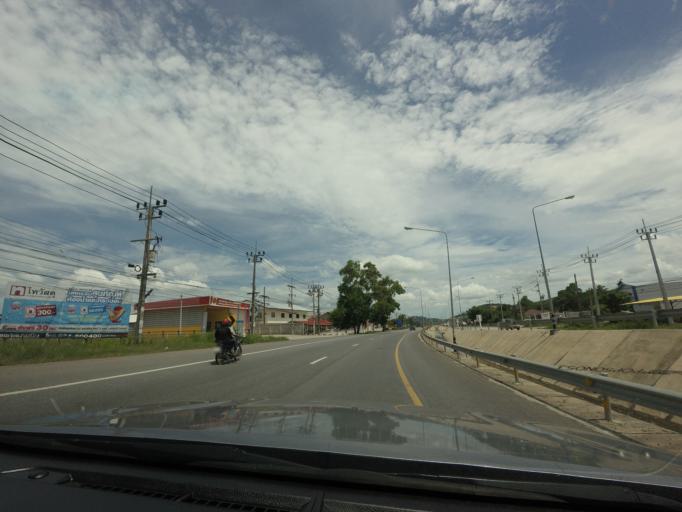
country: TH
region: Songkhla
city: Ban Mai
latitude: 7.2101
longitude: 100.5572
